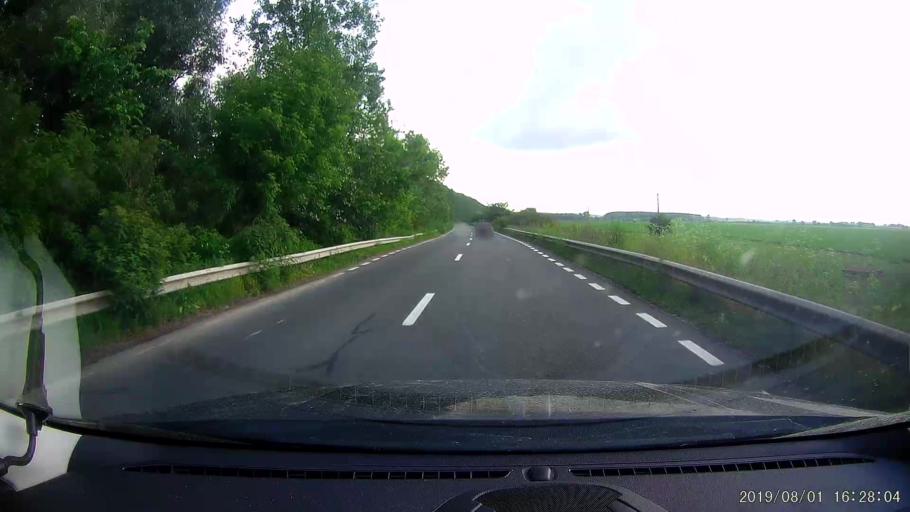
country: RO
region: Calarasi
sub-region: Municipiul Calarasi
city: Calarasi
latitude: 44.1539
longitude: 27.3142
